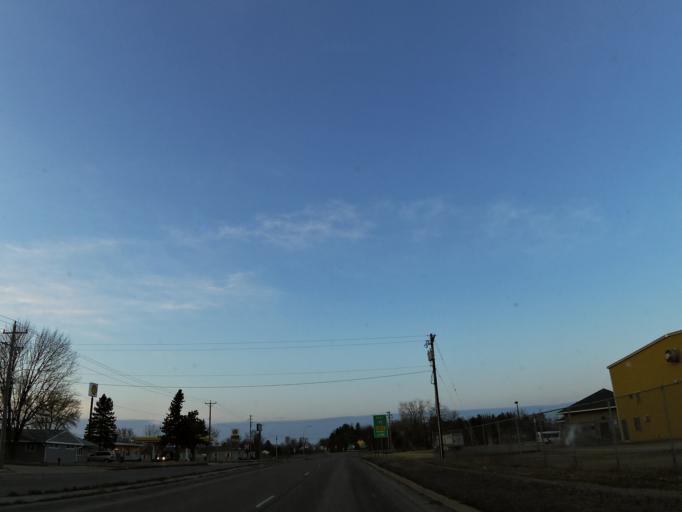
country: US
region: Minnesota
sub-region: Mower County
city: Austin
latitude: 43.6714
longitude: -92.9395
